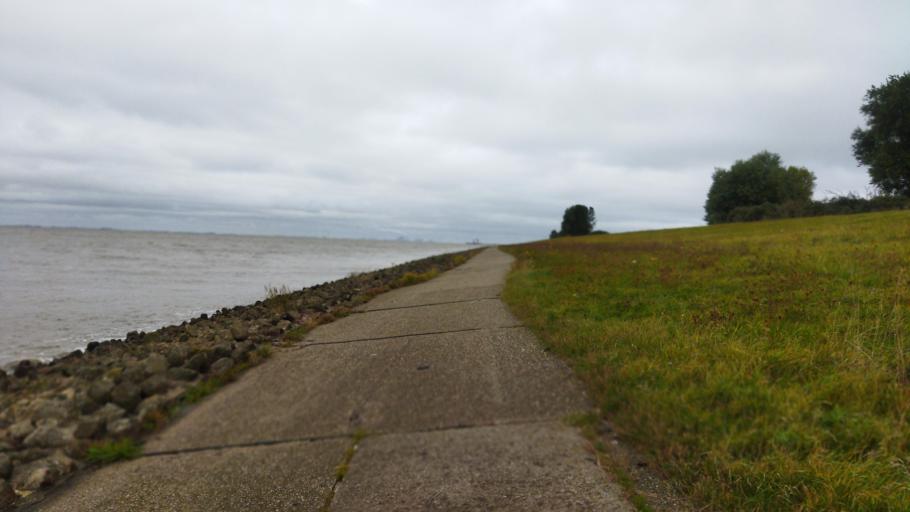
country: NL
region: Groningen
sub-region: Gemeente Delfzijl
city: Delfzijl
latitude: 53.3407
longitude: 7.0175
